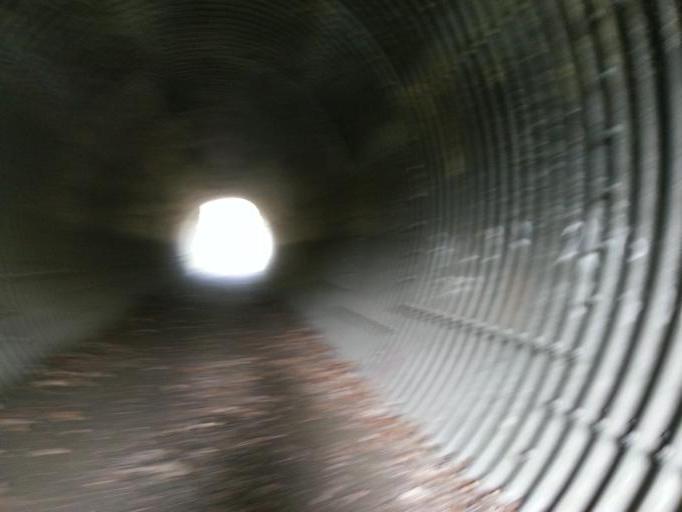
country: NO
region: Sor-Trondelag
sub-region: Trondheim
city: Trondheim
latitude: 63.3887
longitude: 10.3594
